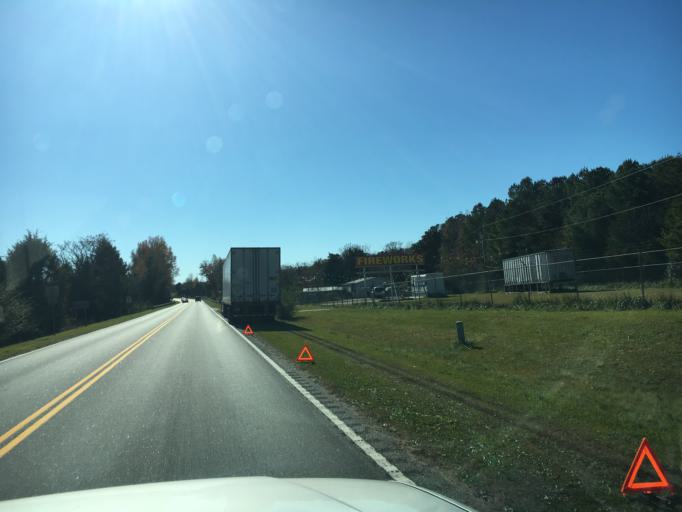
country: US
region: Georgia
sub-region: Hart County
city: Reed Creek
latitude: 34.3913
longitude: -82.8088
